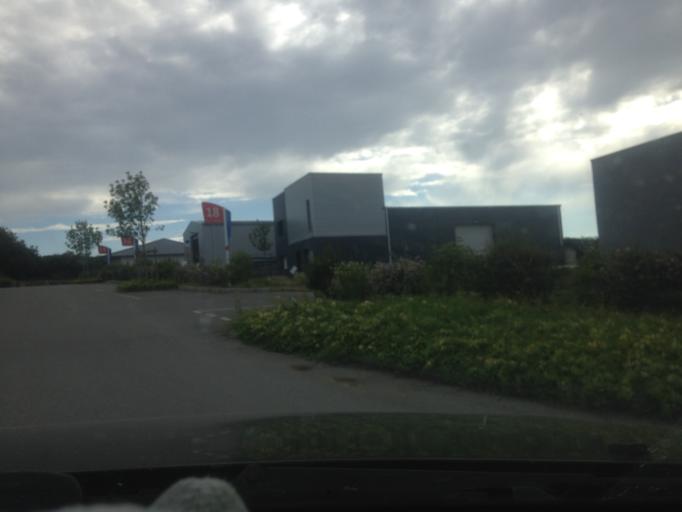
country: FR
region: Brittany
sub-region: Departement du Morbihan
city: Carnac
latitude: 47.5891
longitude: -3.0609
